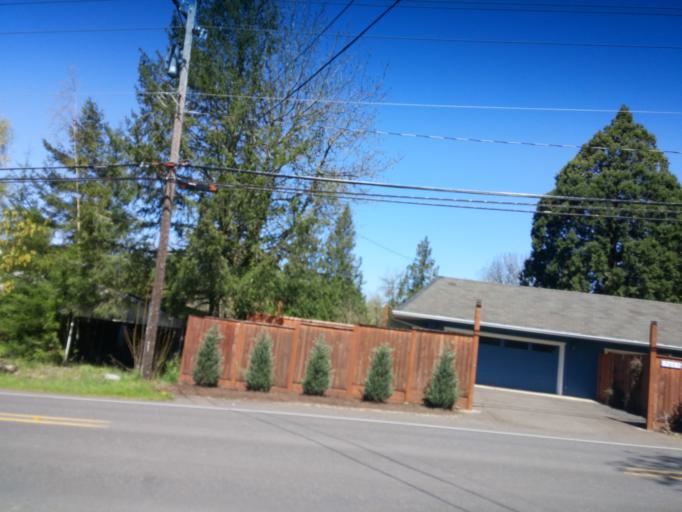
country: US
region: Oregon
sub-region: Washington County
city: West Haven
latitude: 45.5260
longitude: -122.7889
